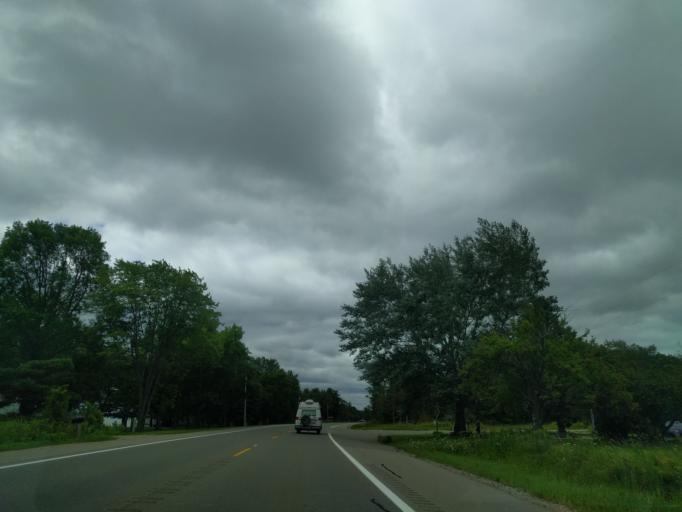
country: US
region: Michigan
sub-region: Menominee County
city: Menominee
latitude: 45.2453
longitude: -87.4924
